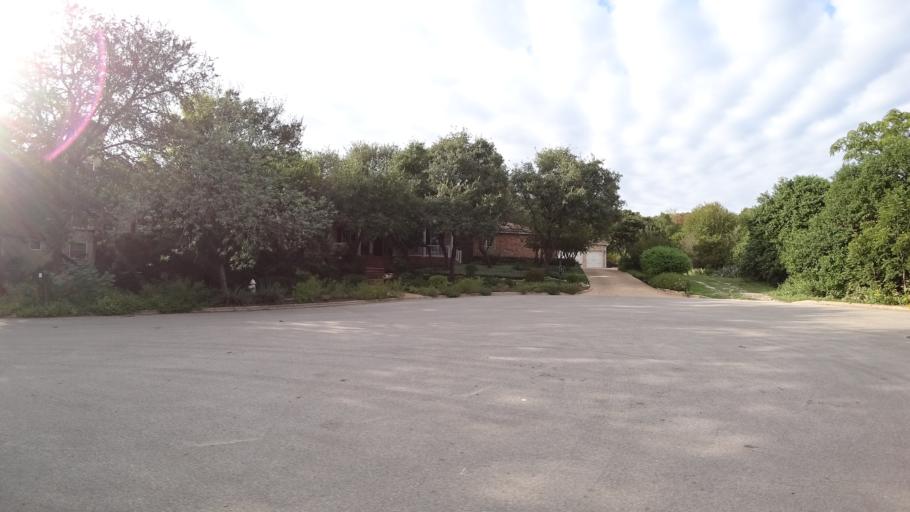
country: US
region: Texas
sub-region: Travis County
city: Rollingwood
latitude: 30.2788
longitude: -97.7833
